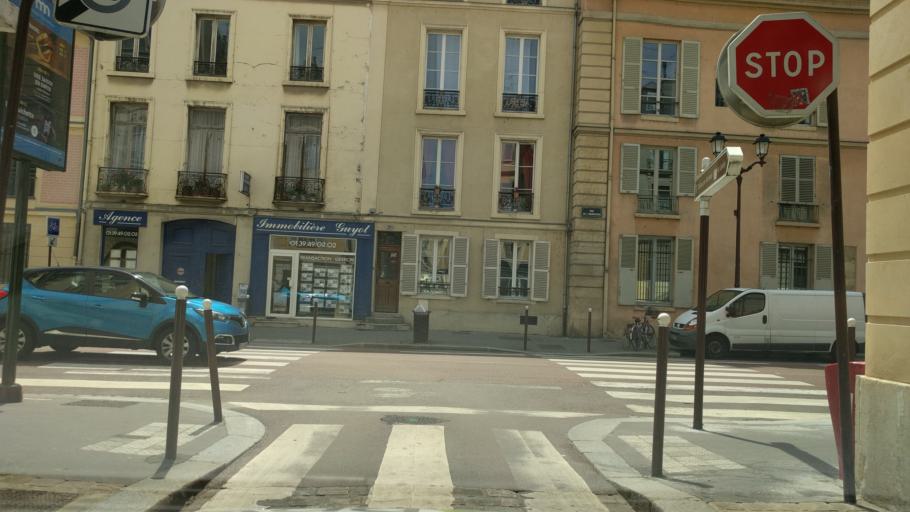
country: FR
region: Ile-de-France
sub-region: Departement des Yvelines
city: Versailles
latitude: 48.8004
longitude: 2.1223
